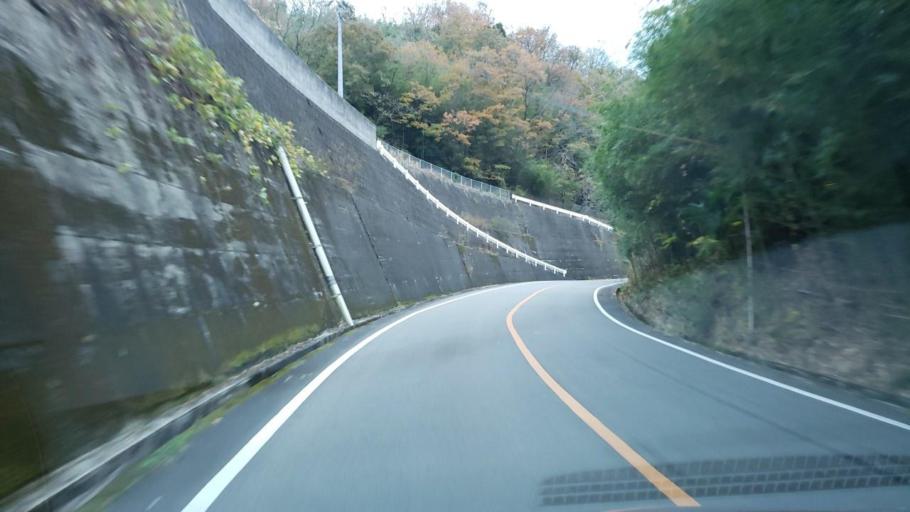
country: JP
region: Tokushima
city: Wakimachi
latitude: 34.0880
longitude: 134.1792
